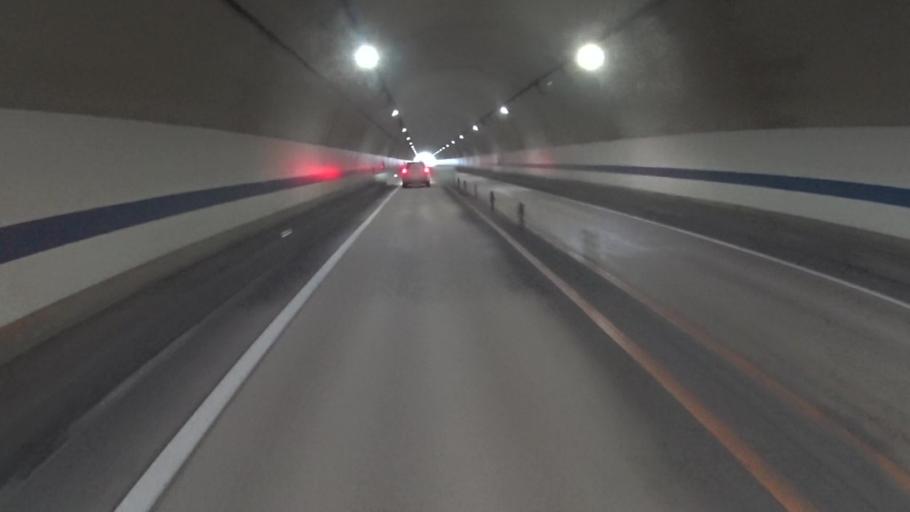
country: JP
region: Kyoto
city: Ayabe
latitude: 35.3734
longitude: 135.2759
